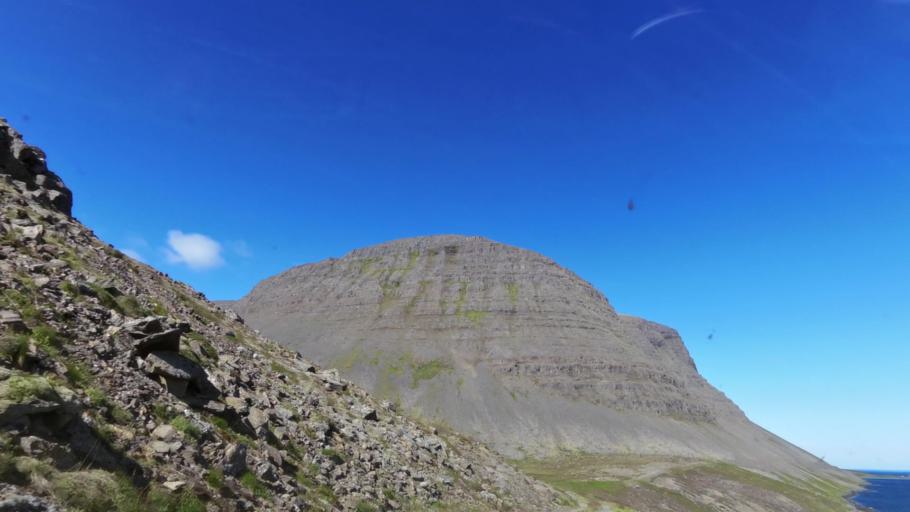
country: IS
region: West
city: Olafsvik
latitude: 65.6246
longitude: -23.8910
